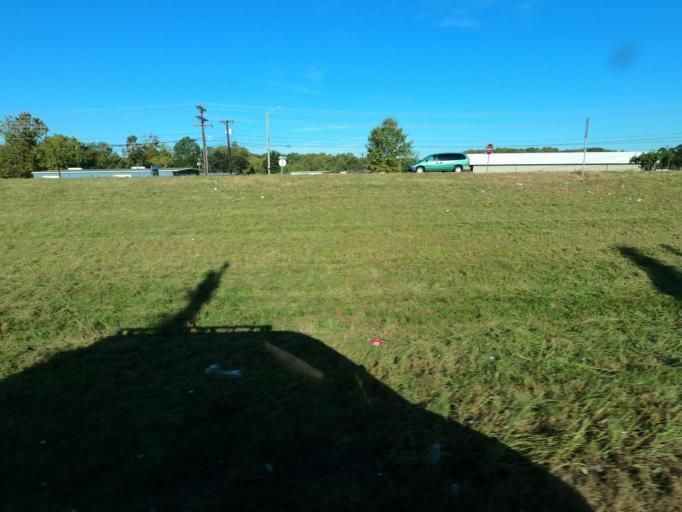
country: US
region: Tennessee
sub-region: Tipton County
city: Munford
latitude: 35.4119
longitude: -89.8309
